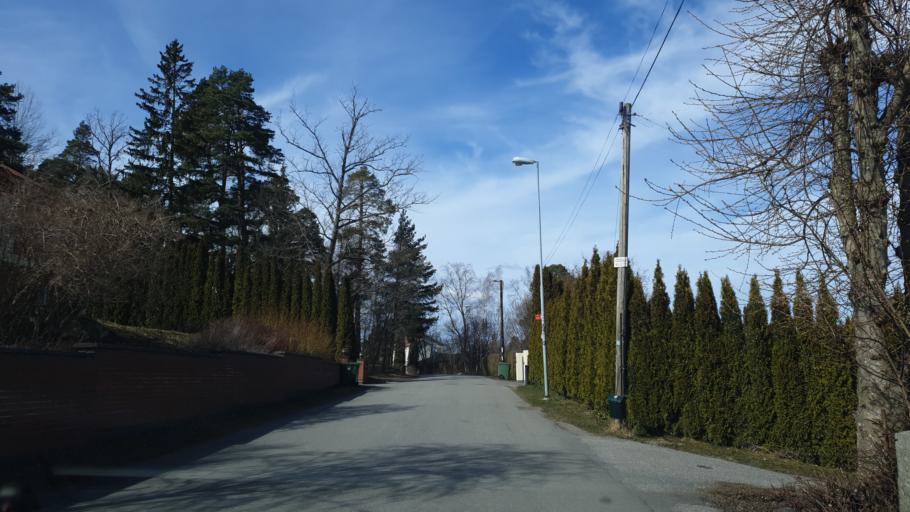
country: SE
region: Stockholm
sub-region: Sollentuna Kommun
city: Sollentuna
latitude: 59.4181
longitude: 17.9841
